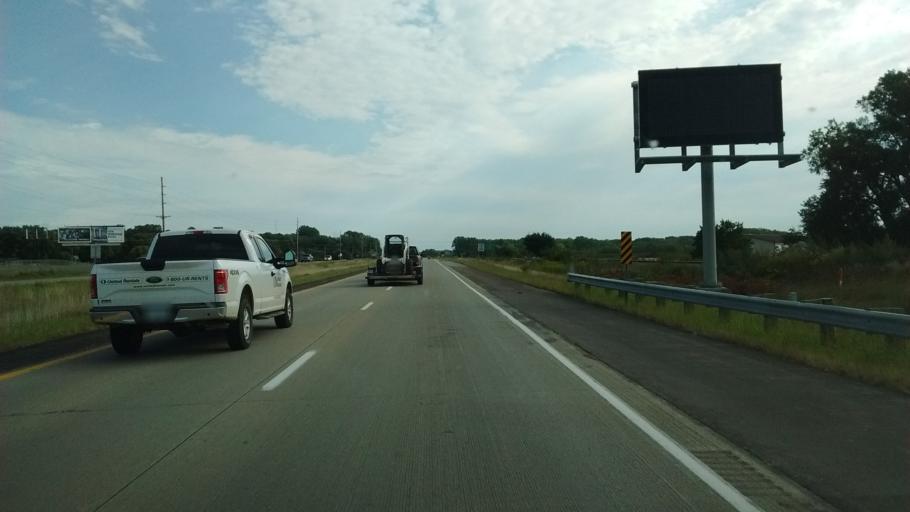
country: US
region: Iowa
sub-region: Woodbury County
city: Sioux City
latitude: 42.5617
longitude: -96.3314
